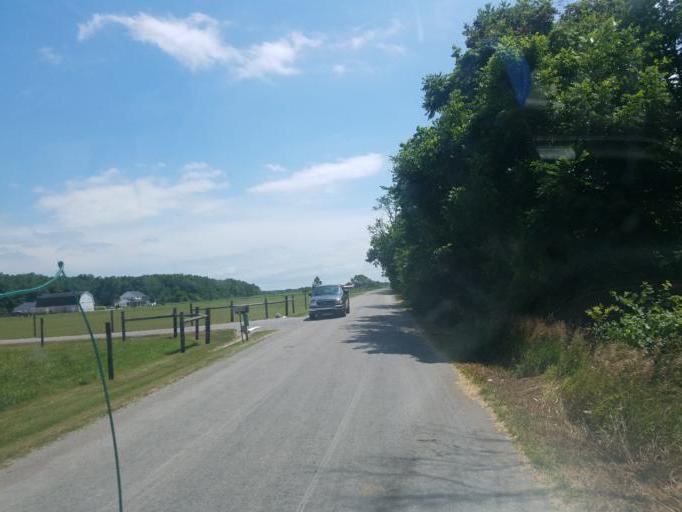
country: US
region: Indiana
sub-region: Allen County
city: Harlan
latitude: 41.1818
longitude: -84.8697
